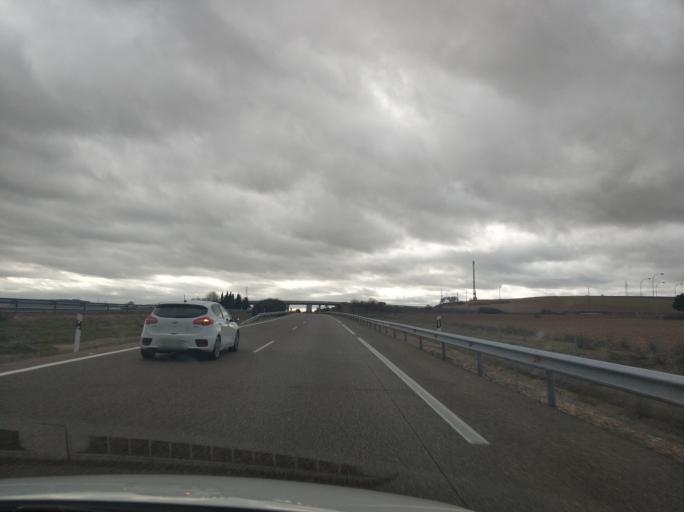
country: ES
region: Castille and Leon
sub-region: Provincia de Palencia
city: Torquemada
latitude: 42.0165
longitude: -4.3447
